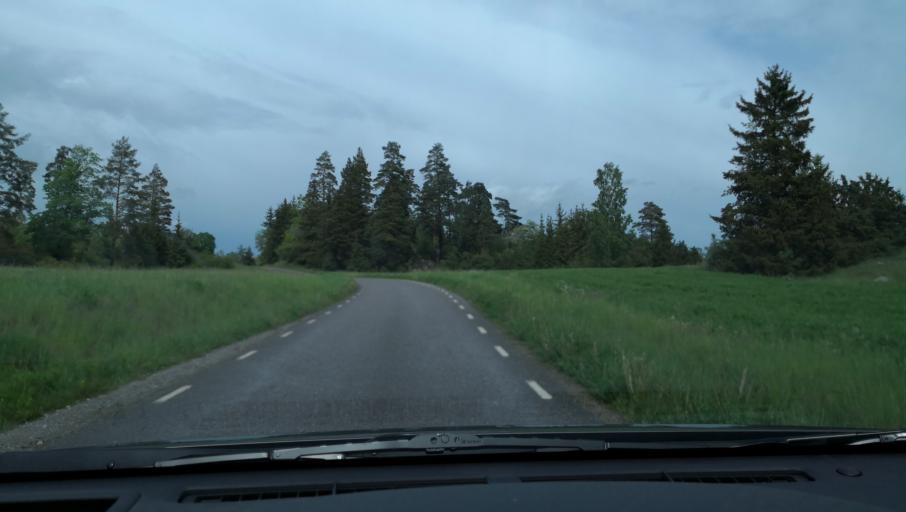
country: SE
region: Uppsala
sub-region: Enkopings Kommun
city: Orsundsbro
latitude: 59.7060
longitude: 17.4212
